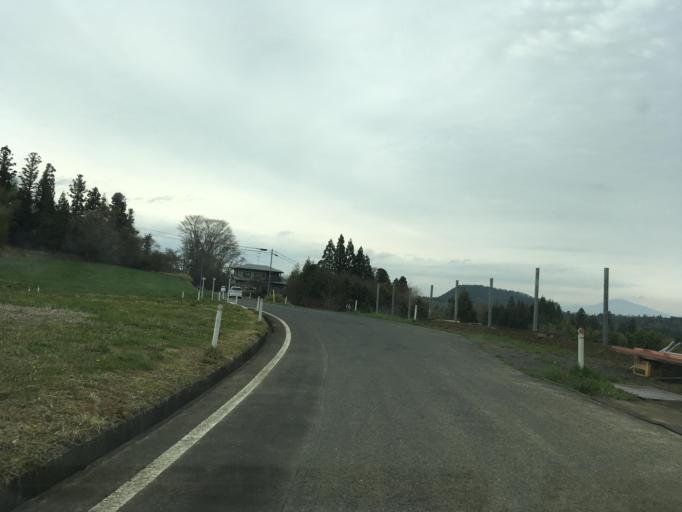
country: JP
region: Iwate
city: Ichinoseki
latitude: 38.8445
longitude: 141.3334
